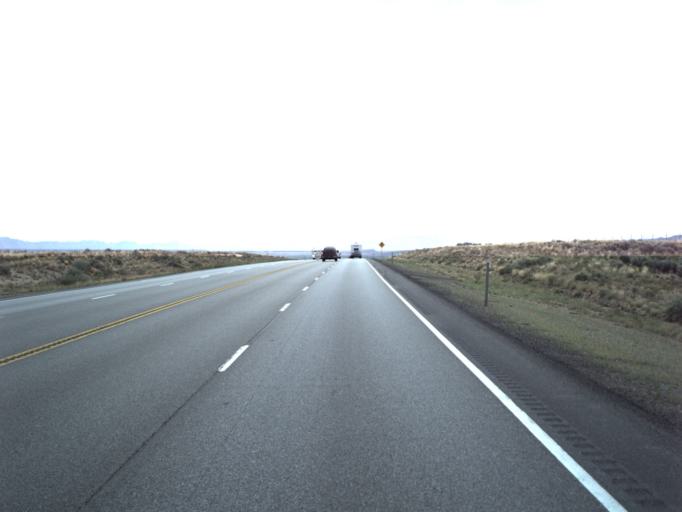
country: US
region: Utah
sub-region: Carbon County
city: East Carbon City
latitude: 39.5052
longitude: -110.5316
